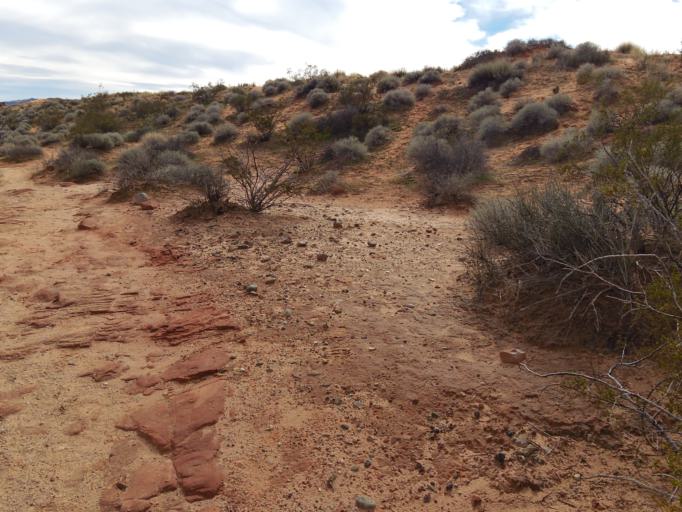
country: US
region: Nevada
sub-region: Clark County
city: Moapa Valley
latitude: 36.4869
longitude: -114.5246
